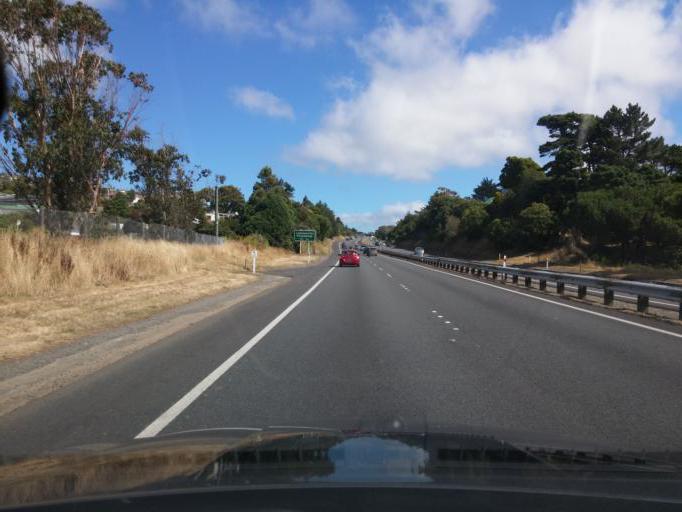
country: NZ
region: Wellington
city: Petone
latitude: -41.2097
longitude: 174.8161
